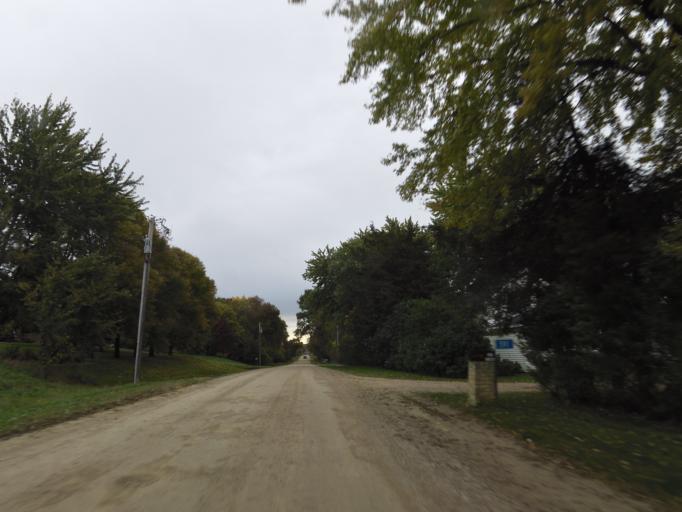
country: US
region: Minnesota
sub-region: Scott County
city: Prior Lake
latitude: 44.7036
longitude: -93.5085
